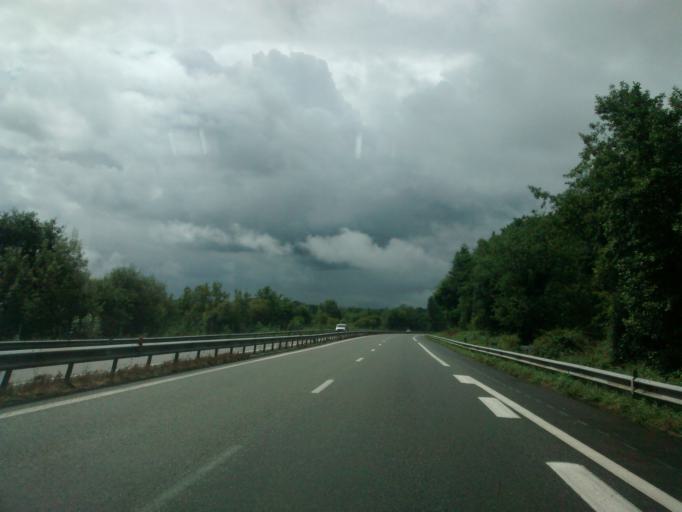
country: FR
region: Aquitaine
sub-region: Departement des Pyrenees-Atlantiques
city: Urt
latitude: 43.4623
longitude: -1.2897
